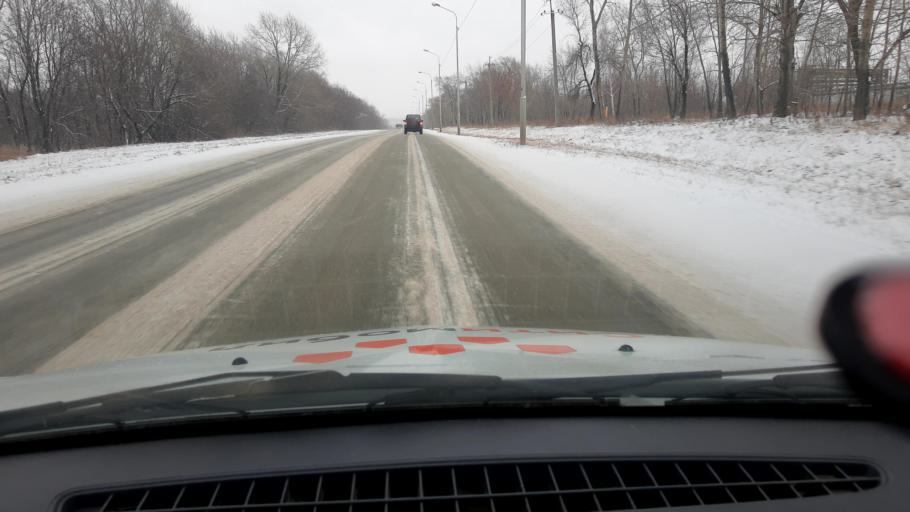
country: RU
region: Bashkortostan
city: Blagoveshchensk
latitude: 54.8982
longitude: 56.0875
